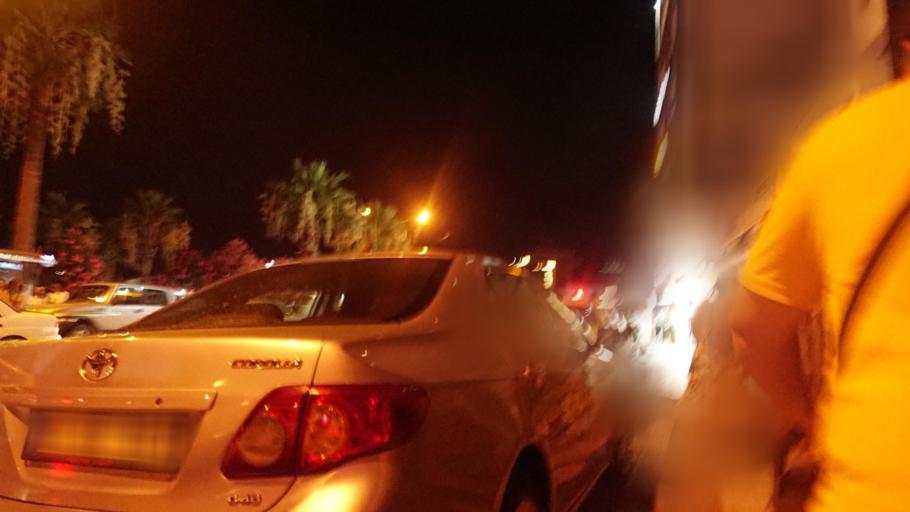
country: TR
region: Aydin
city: Kusadasi
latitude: 37.8625
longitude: 27.2607
